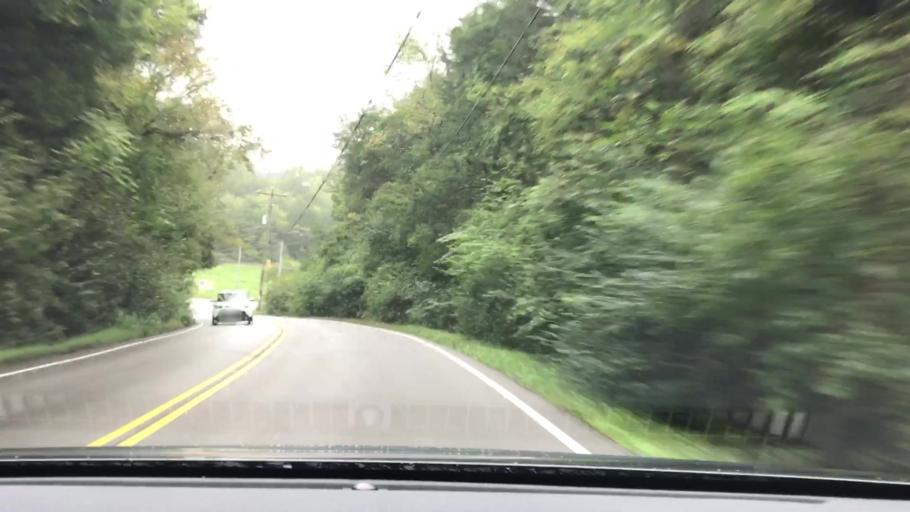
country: US
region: Tennessee
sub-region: Williamson County
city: Nolensville
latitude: 36.0119
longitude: -86.7049
